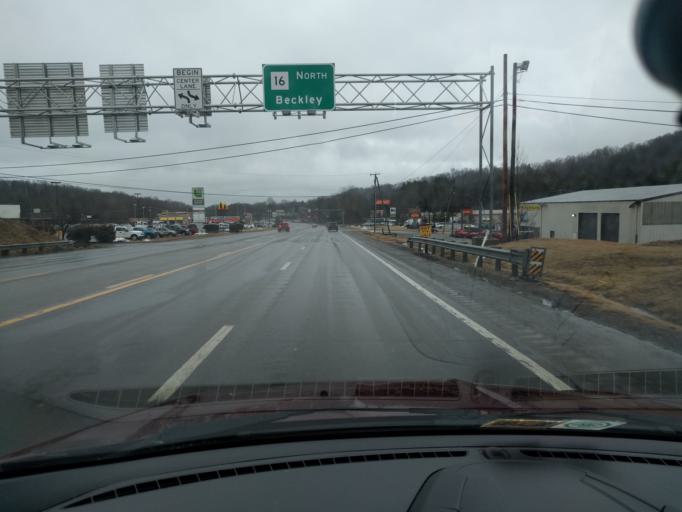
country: US
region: West Virginia
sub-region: Raleigh County
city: Sophia
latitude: 37.7263
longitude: -81.2455
